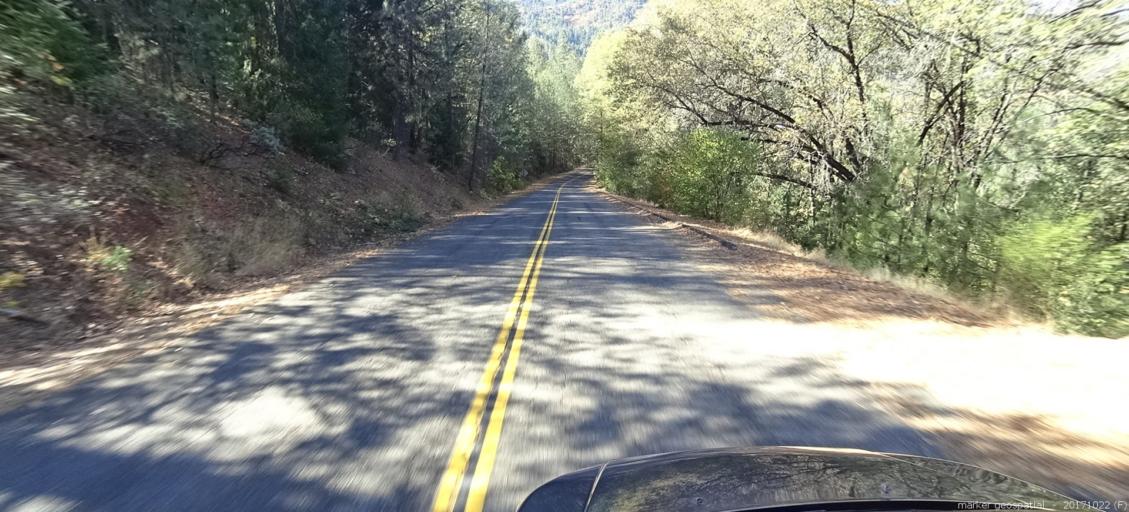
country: US
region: California
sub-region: Shasta County
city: Central Valley (historical)
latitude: 40.9210
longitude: -122.4036
